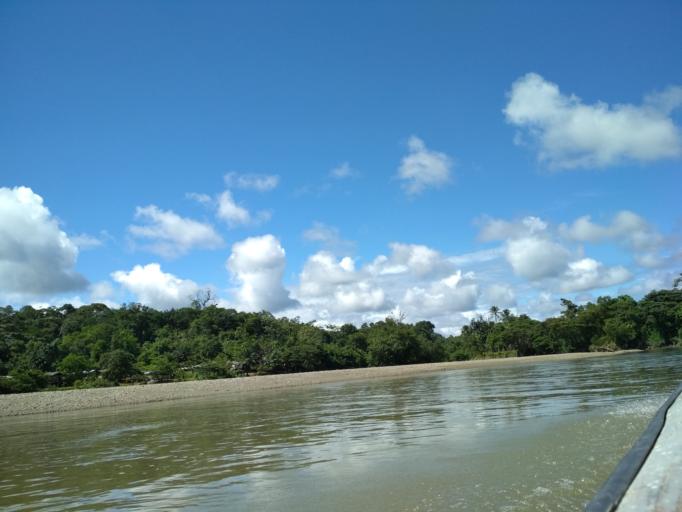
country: CO
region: Cauca
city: Timbiqui
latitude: 2.7613
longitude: -77.6633
